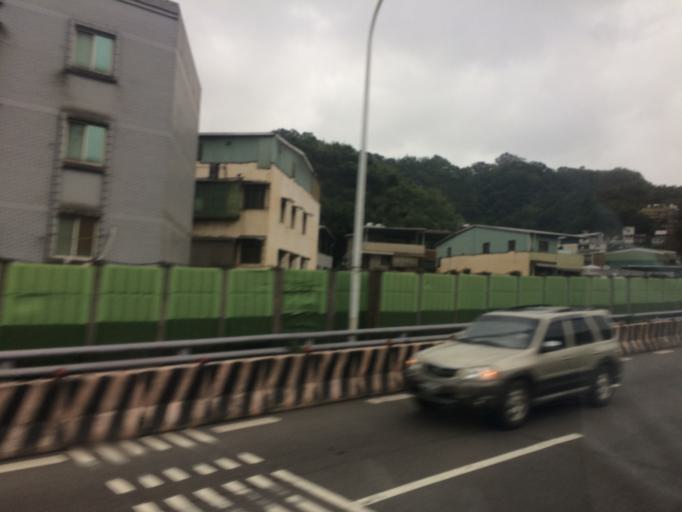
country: TW
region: Taiwan
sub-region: Keelung
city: Keelung
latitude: 25.1250
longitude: 121.7371
